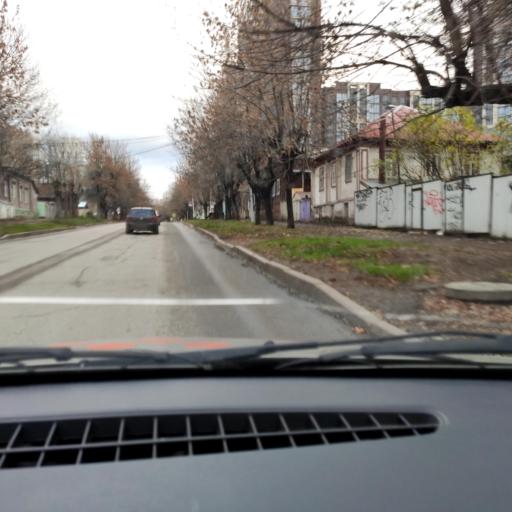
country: RU
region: Bashkortostan
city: Ufa
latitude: 54.7188
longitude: 55.9635
